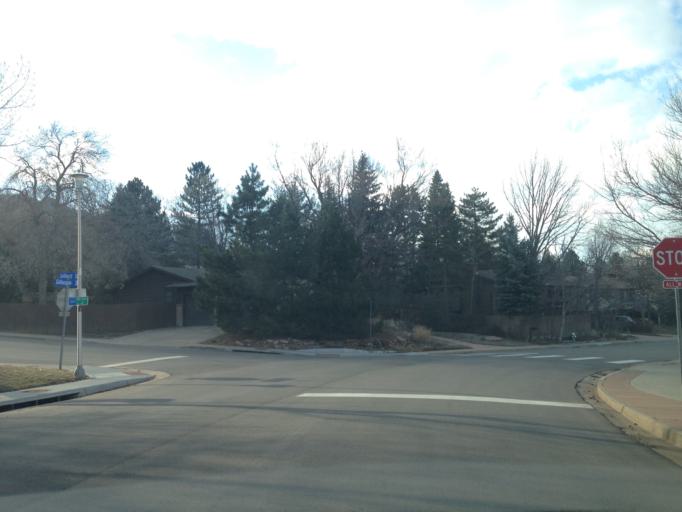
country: US
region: Colorado
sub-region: Boulder County
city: Boulder
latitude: 39.9710
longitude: -105.2520
